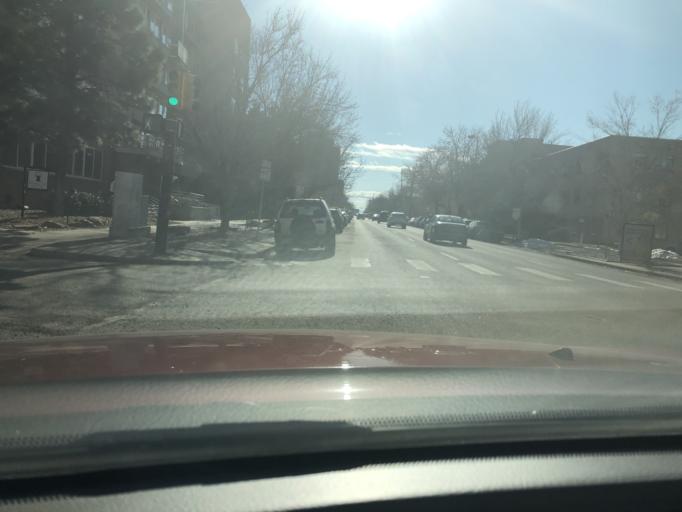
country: US
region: Colorado
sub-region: Denver County
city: Denver
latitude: 39.7354
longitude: -104.9836
